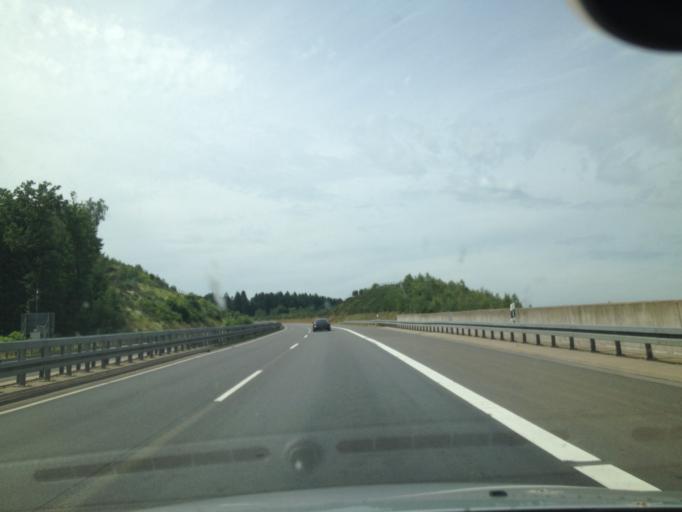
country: DE
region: North Rhine-Westphalia
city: Kreuztal
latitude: 50.9705
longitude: 7.9745
